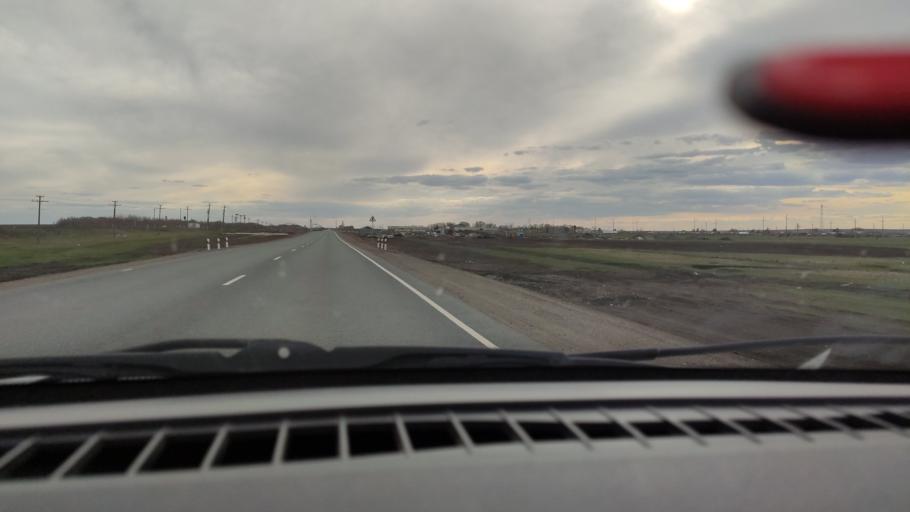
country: RU
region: Bashkortostan
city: Mayachnyy
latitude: 52.3592
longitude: 55.5860
